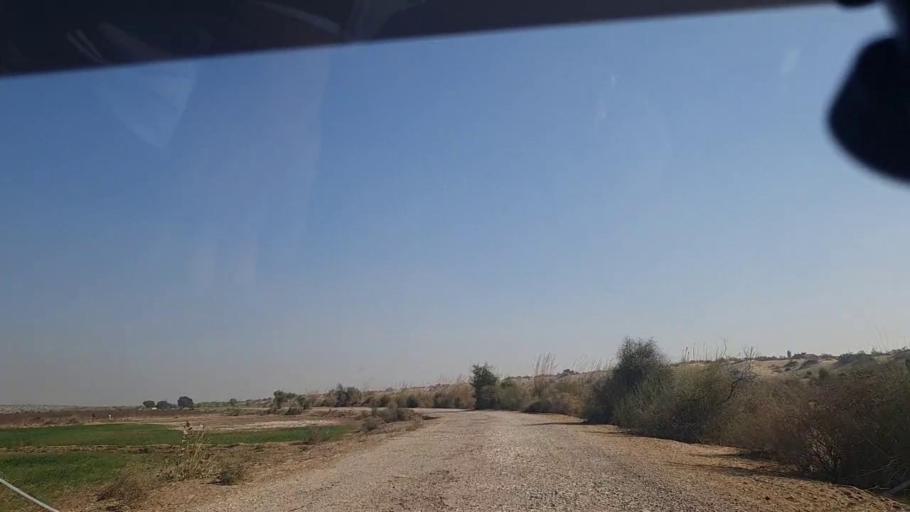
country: PK
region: Sindh
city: Khanpur
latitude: 27.5589
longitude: 69.3271
